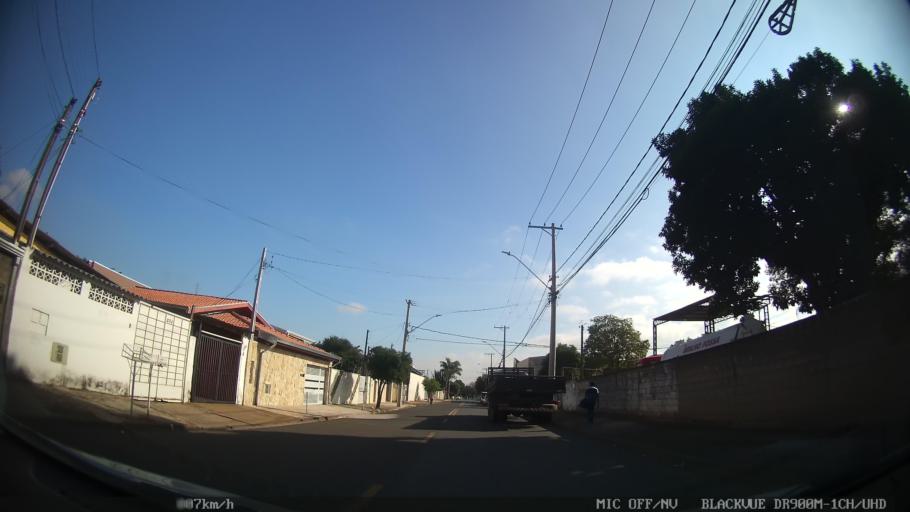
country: BR
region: Sao Paulo
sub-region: Hortolandia
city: Hortolandia
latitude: -22.8948
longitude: -47.1784
